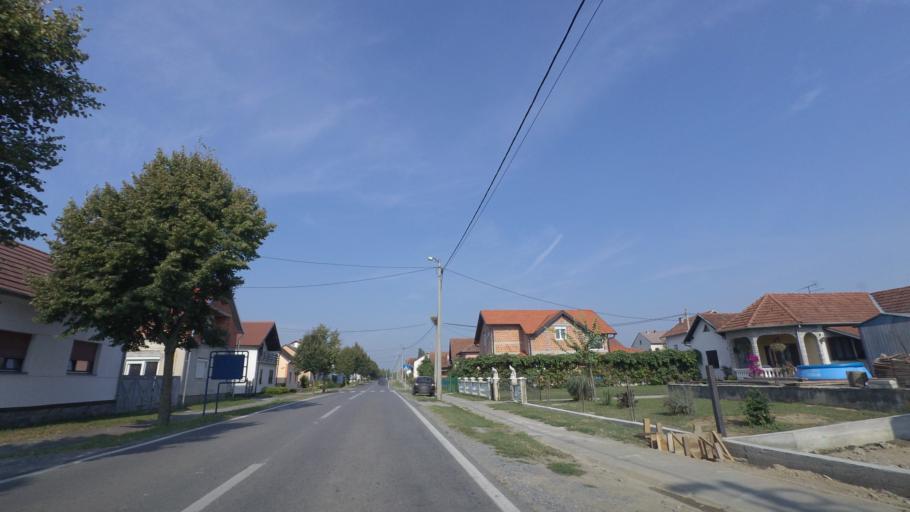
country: HR
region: Pozesko-Slavonska
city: Lipik
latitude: 45.4152
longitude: 17.1528
